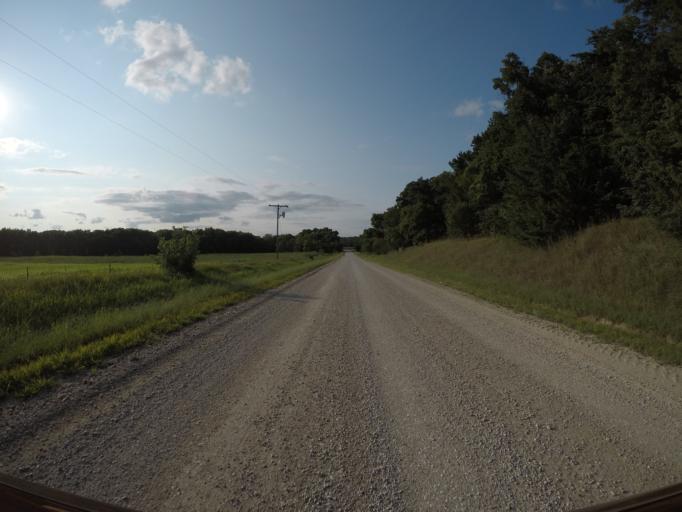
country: US
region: Kansas
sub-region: Wabaunsee County
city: Alma
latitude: 38.9475
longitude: -96.2410
